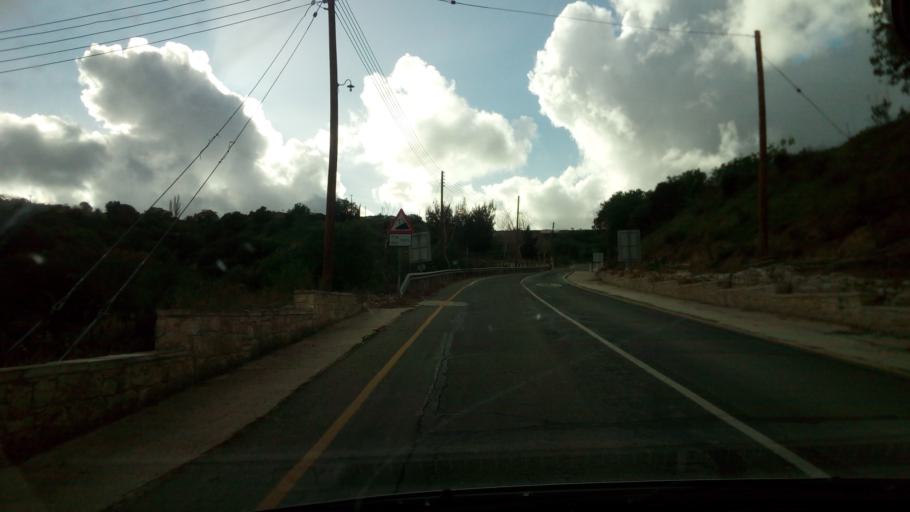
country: CY
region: Pafos
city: Mesogi
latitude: 34.8579
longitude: 32.5065
